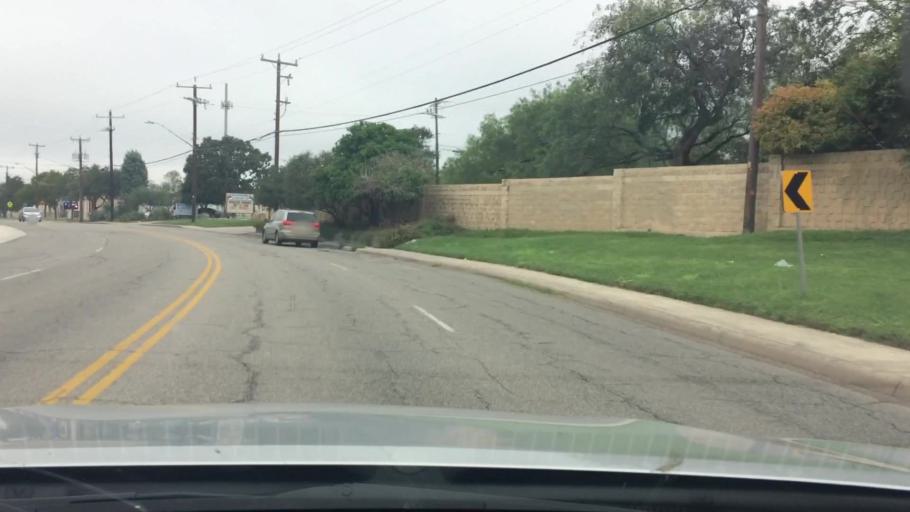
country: US
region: Texas
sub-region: Bexar County
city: Hollywood Park
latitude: 29.5839
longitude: -98.4485
